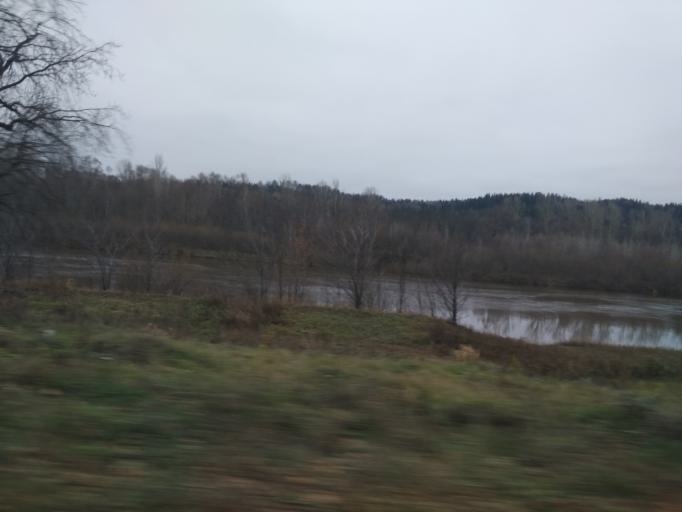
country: RU
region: Kirov
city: Krasnaya Polyana
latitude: 56.2446
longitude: 51.1842
